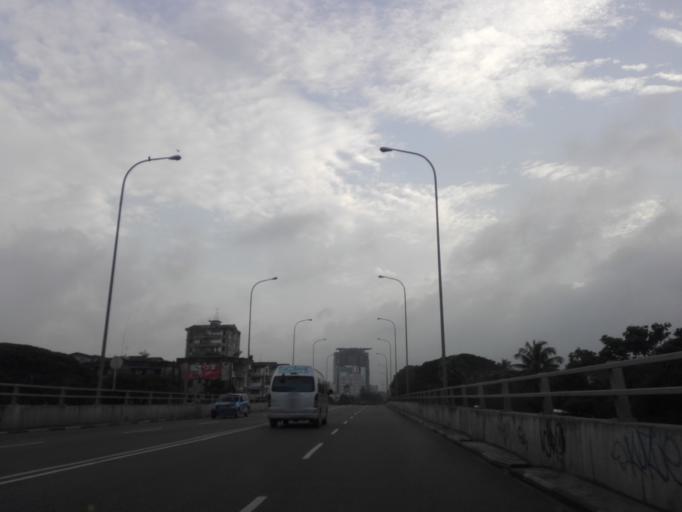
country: MM
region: Yangon
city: Yangon
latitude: 16.8268
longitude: 96.1308
